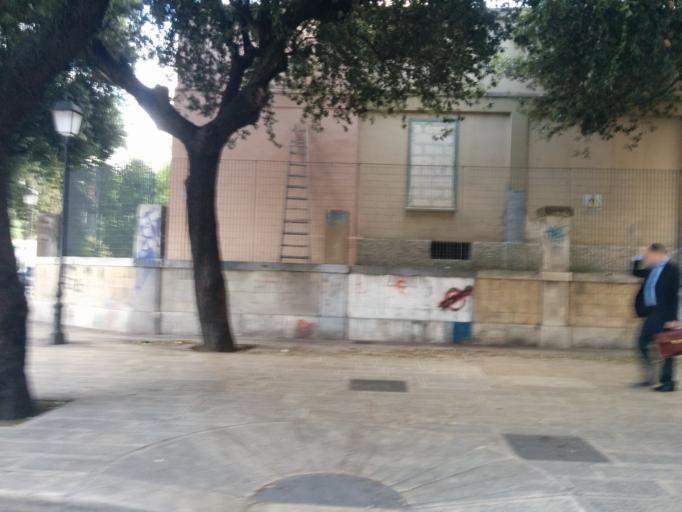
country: IT
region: Apulia
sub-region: Provincia di Taranto
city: Taranto
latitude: 40.4699
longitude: 17.2519
